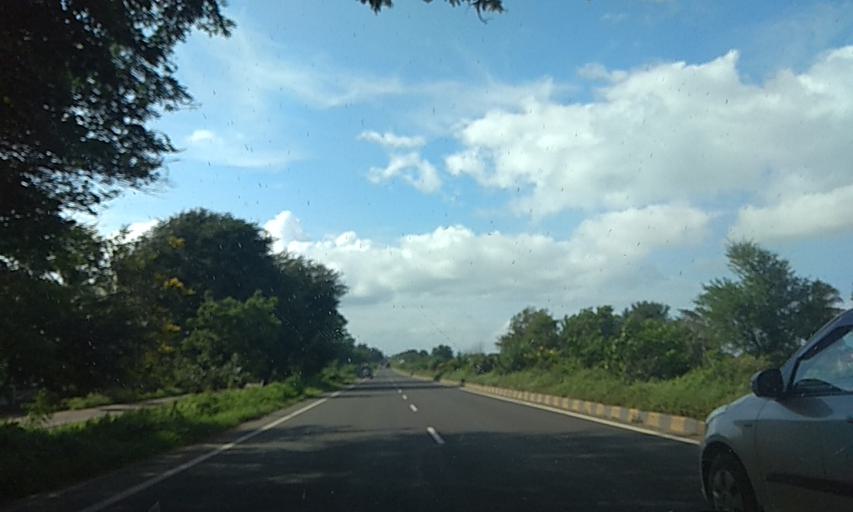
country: IN
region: Maharashtra
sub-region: Kolhapur
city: Kodoli
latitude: 17.0192
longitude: 74.2531
